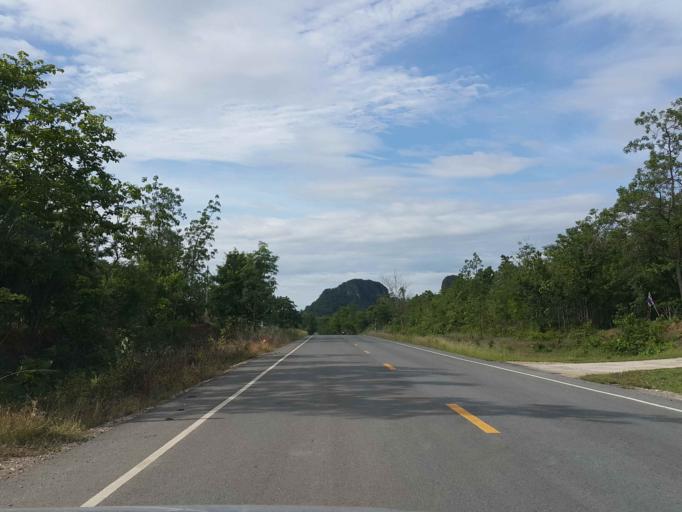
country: TH
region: Sukhothai
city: Thung Saliam
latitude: 17.2972
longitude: 99.5270
